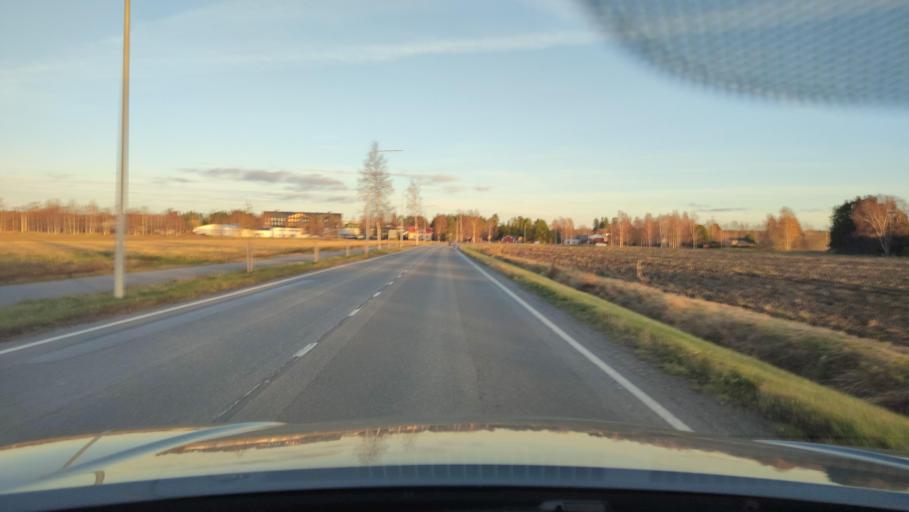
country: FI
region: Ostrobothnia
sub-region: Sydosterbotten
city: Naerpes
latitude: 62.4722
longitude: 21.3438
